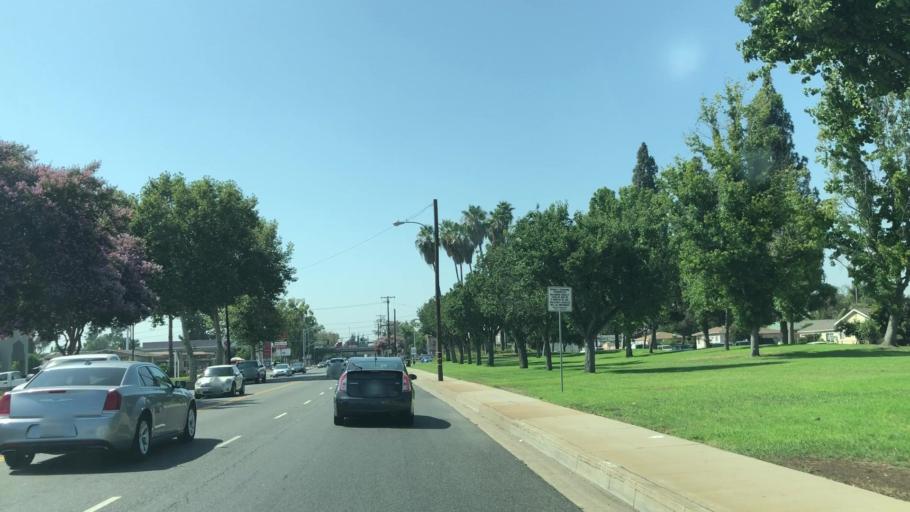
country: US
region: California
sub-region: Los Angeles County
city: West Whittier-Los Nietos
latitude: 33.9911
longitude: -118.0657
